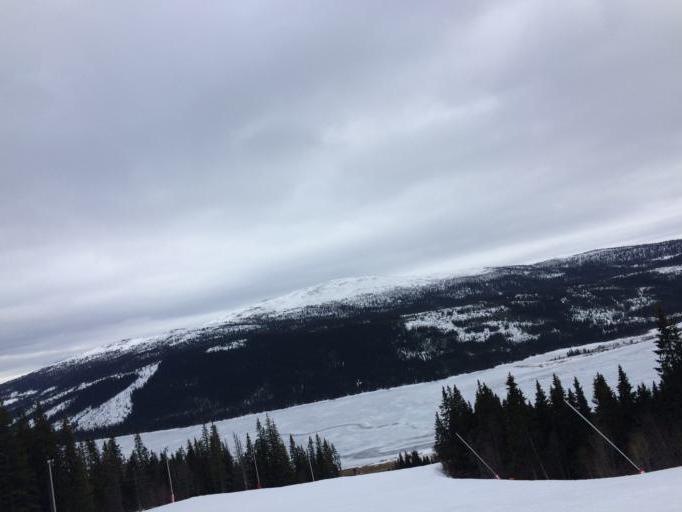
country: SE
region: Jaemtland
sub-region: Are Kommun
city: Are
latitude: 63.4104
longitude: 13.0568
